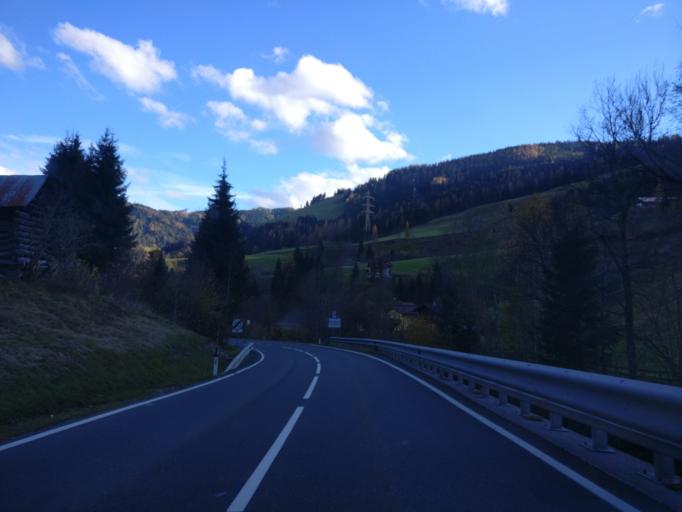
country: AT
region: Salzburg
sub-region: Politischer Bezirk Sankt Johann im Pongau
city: Muhlbach am Hochkonig
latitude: 47.3788
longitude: 13.1135
